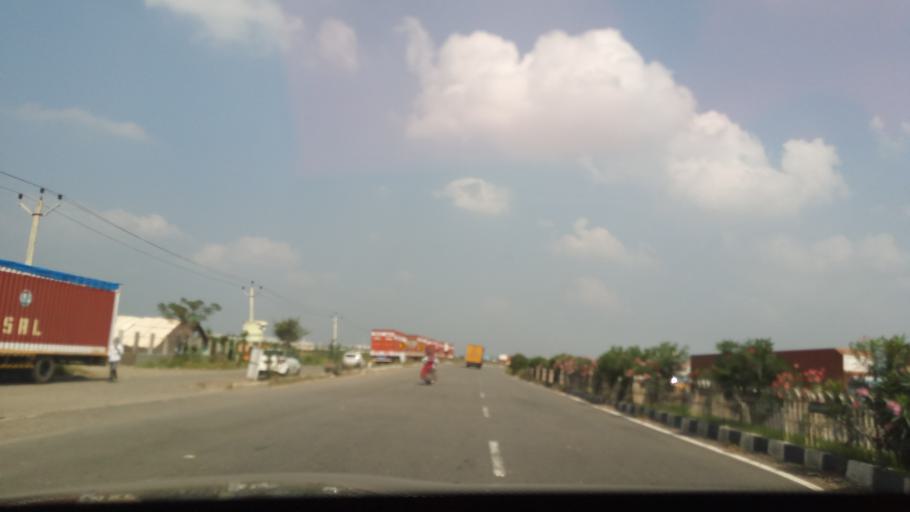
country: IN
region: Tamil Nadu
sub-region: Kancheepuram
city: Sriperumbudur
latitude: 12.8978
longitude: 79.9314
